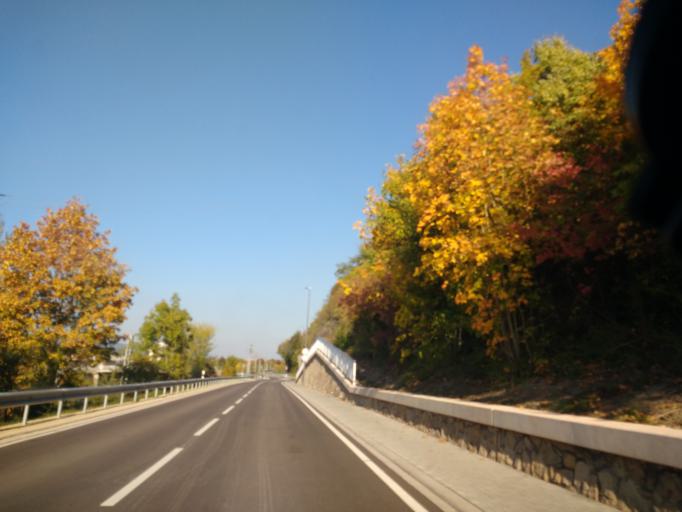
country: DE
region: Rheinland-Pfalz
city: Konz
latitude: 49.7103
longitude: 6.5977
